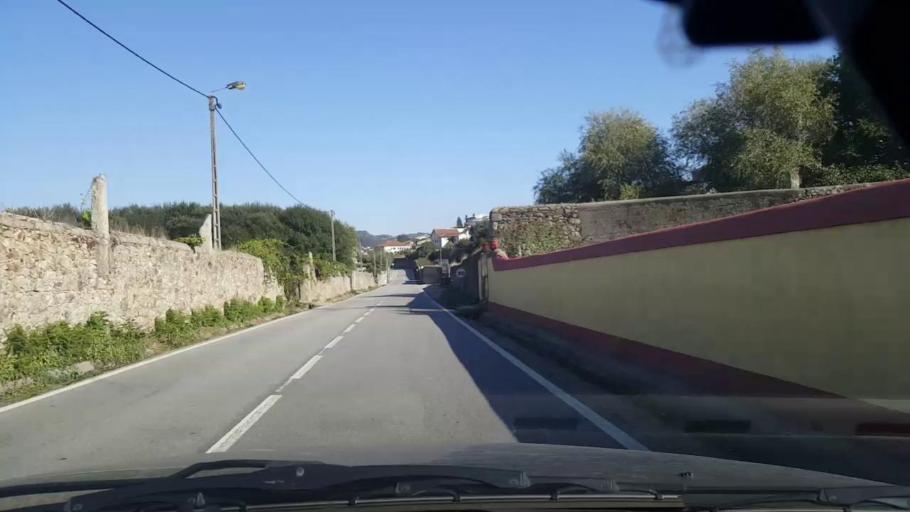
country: PT
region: Porto
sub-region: Vila do Conde
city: Arvore
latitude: 41.3346
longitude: -8.6707
